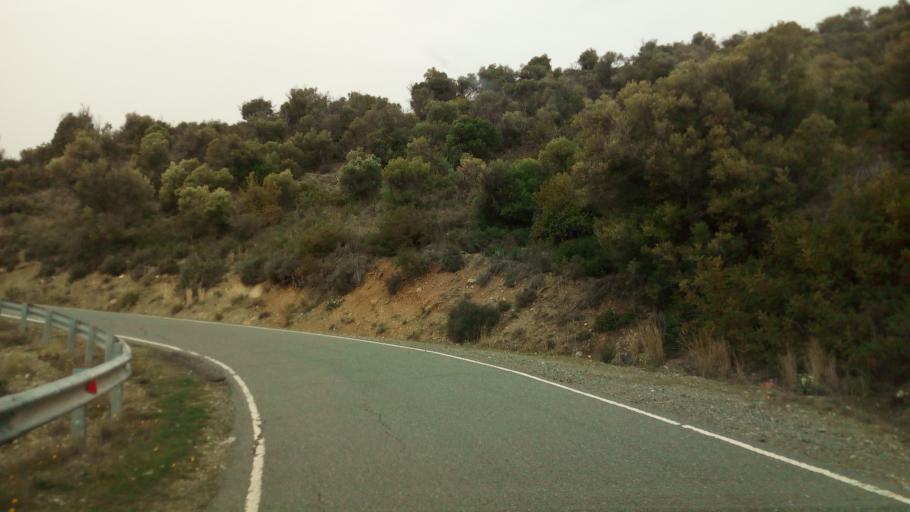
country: CY
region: Limassol
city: Mouttagiaka
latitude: 34.7966
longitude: 33.0851
